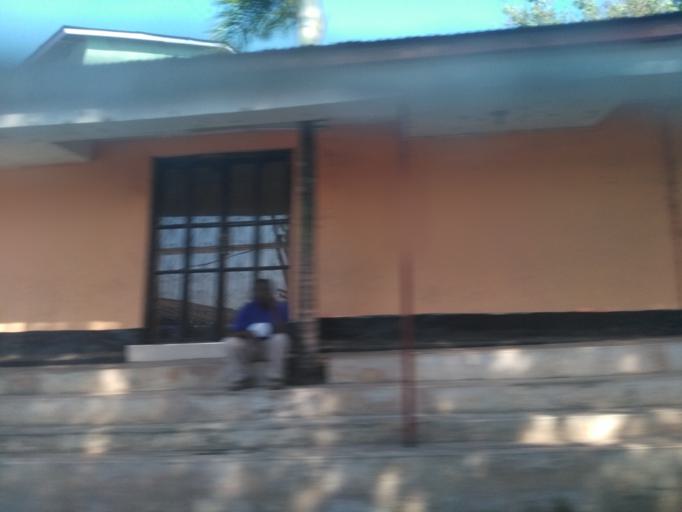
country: TZ
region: Mwanza
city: Mwanza
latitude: -2.4996
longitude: 32.8968
